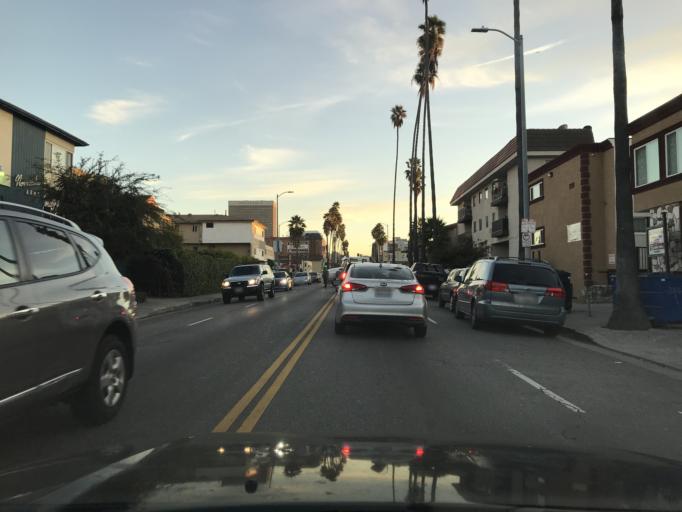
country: US
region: California
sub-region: Los Angeles County
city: Silver Lake
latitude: 34.0703
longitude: -118.3004
